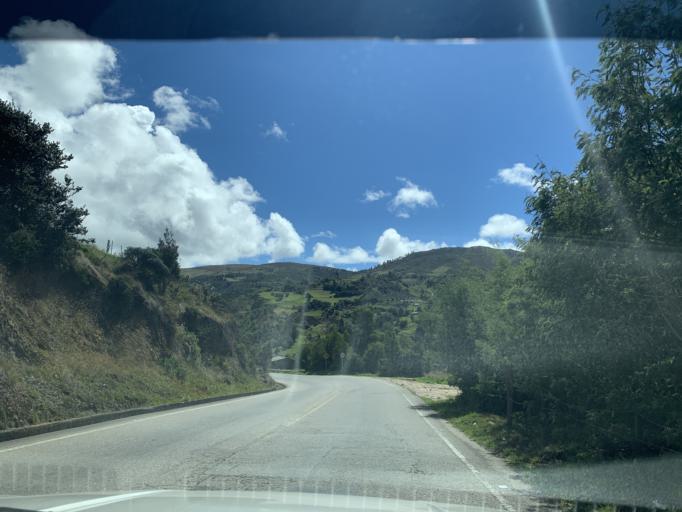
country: CO
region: Boyaca
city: Aquitania
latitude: 5.6129
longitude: -72.8790
